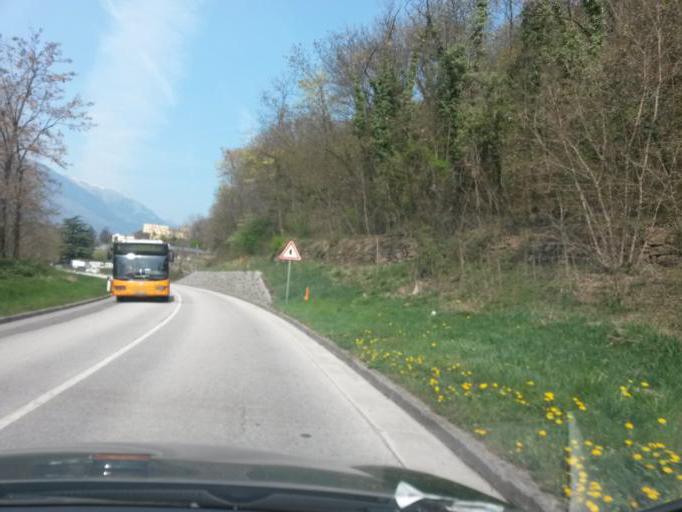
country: IT
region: Trentino-Alto Adige
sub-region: Bolzano
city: Sinigo
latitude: 46.6554
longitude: 11.1857
